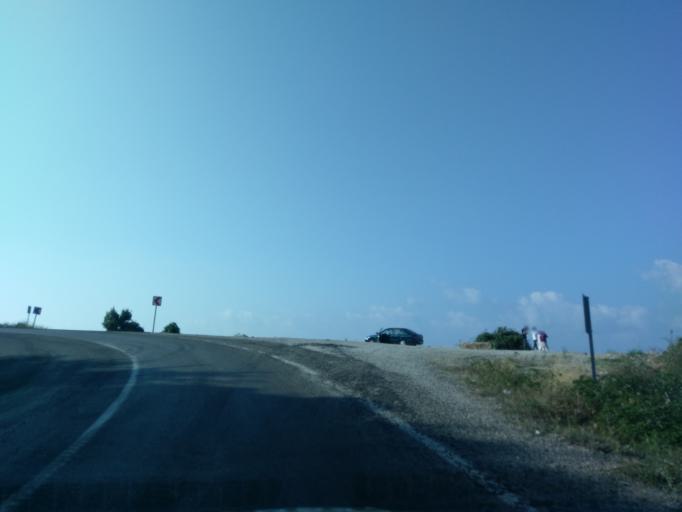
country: TR
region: Sinop
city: Ayancik
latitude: 41.9416
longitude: 34.6772
